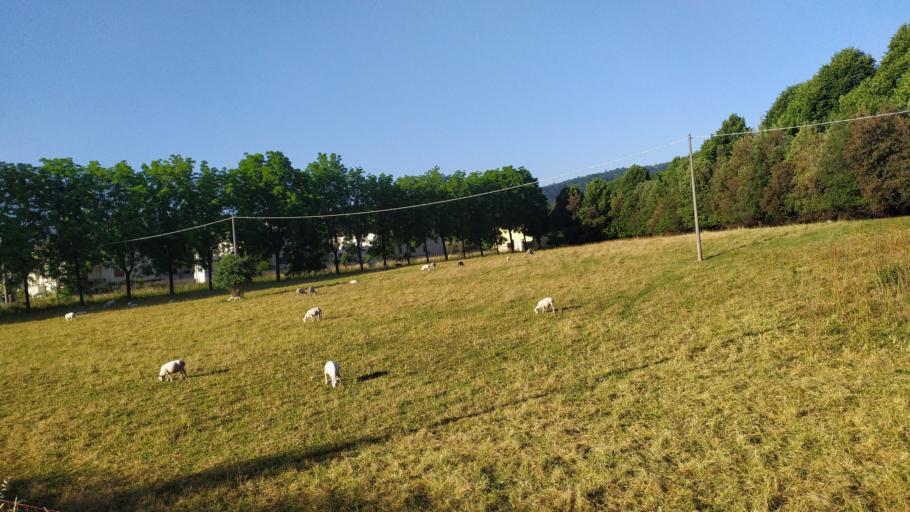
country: IT
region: Veneto
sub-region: Provincia di Vicenza
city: Malo
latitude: 45.6409
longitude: 11.4227
